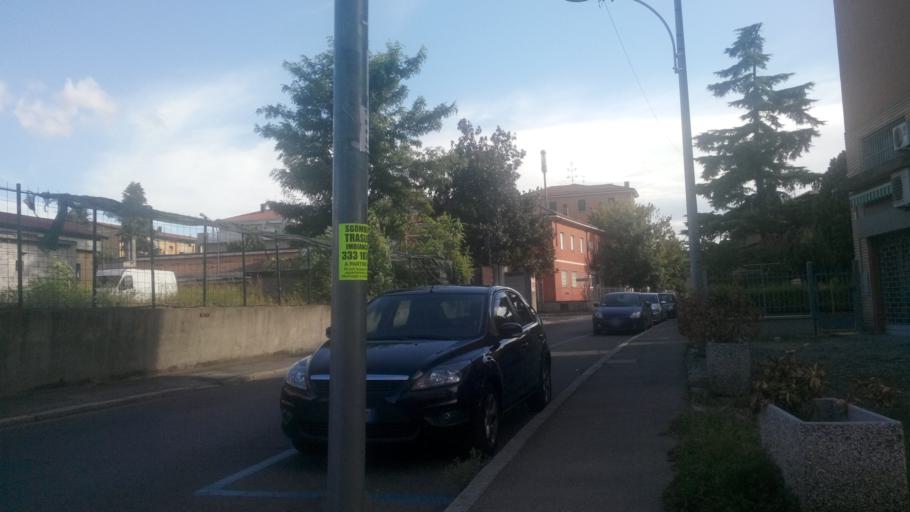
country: IT
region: Emilia-Romagna
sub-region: Provincia di Bologna
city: Bologna
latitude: 44.5213
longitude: 11.3516
